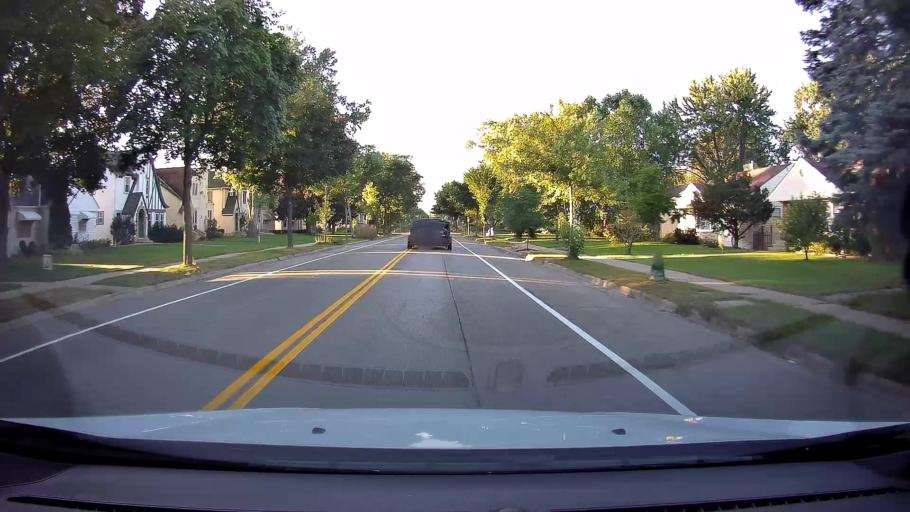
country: US
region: Minnesota
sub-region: Hennepin County
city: Richfield
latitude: 44.9225
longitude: -93.2473
